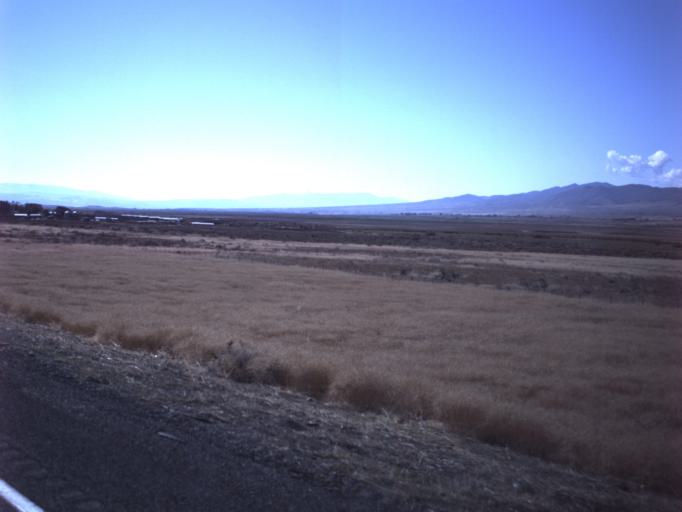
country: US
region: Utah
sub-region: Sanpete County
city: Gunnison
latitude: 39.2732
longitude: -111.8740
